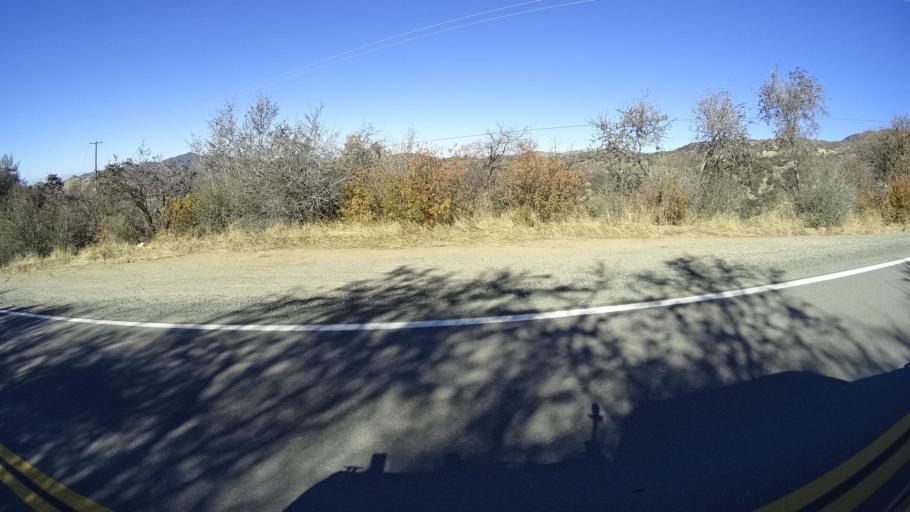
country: US
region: California
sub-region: Kern County
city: Alta Sierra
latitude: 35.7381
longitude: -118.6368
